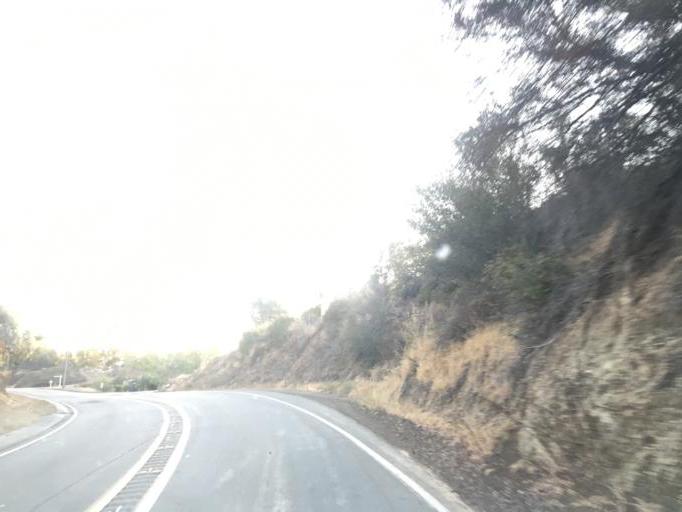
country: US
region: California
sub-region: Los Angeles County
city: Malibu Beach
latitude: 34.0965
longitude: -118.6755
